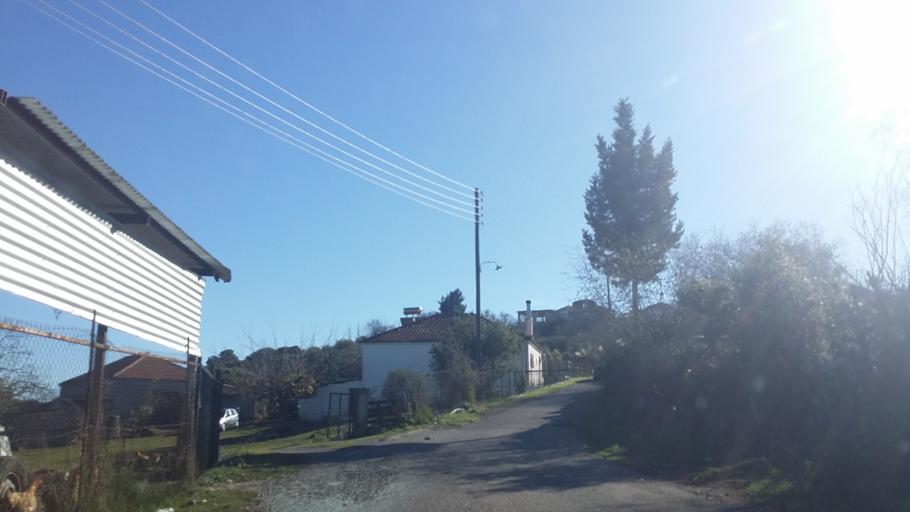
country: GR
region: West Greece
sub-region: Nomos Aitolias kai Akarnanias
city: Fitiai
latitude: 38.7136
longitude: 21.1733
